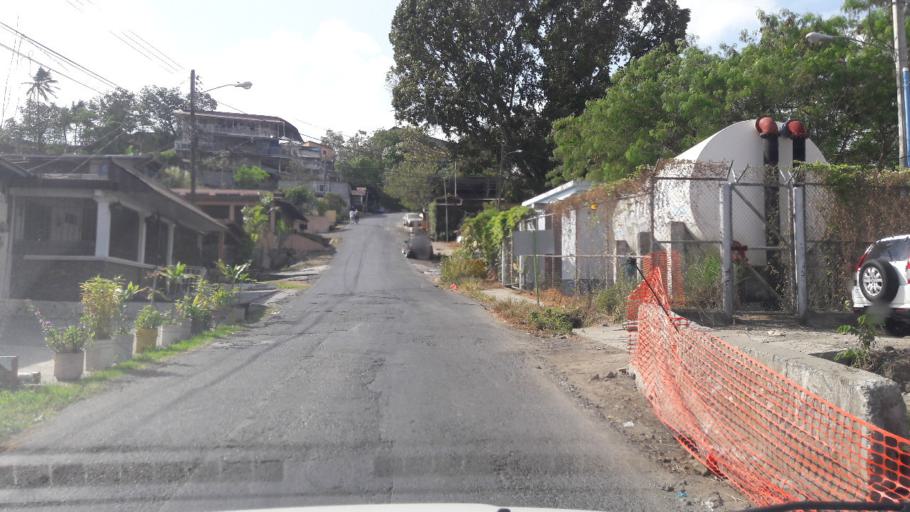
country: PA
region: Panama
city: San Miguelito
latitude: 9.0485
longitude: -79.5102
